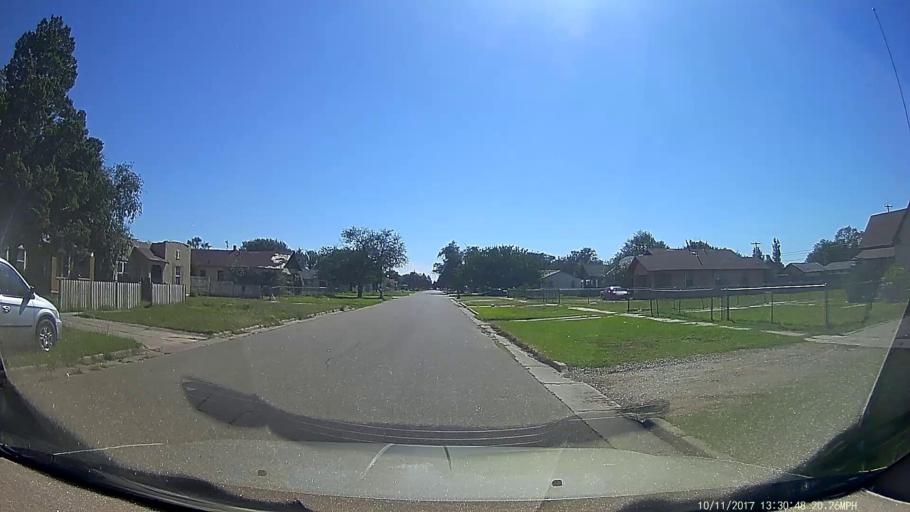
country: US
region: New Mexico
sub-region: Curry County
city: Clovis
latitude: 34.4028
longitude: -103.2117
